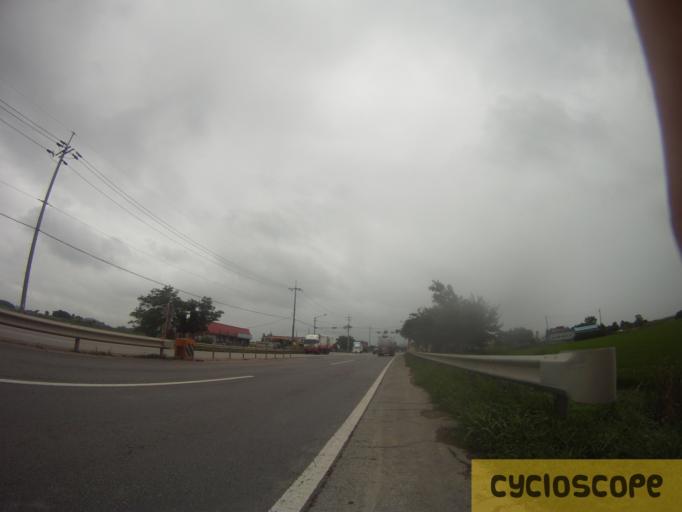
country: KR
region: Gyeonggi-do
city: Hwaseong-si
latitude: 37.0043
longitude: 126.8288
